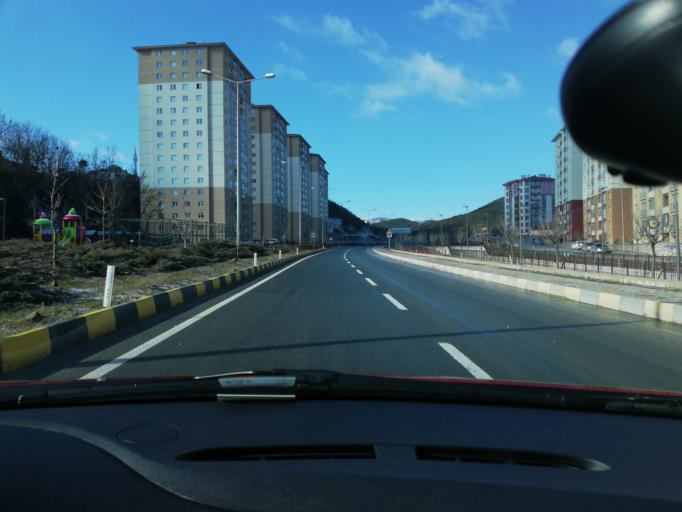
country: TR
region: Kastamonu
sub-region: Cide
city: Kastamonu
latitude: 41.3624
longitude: 33.7615
